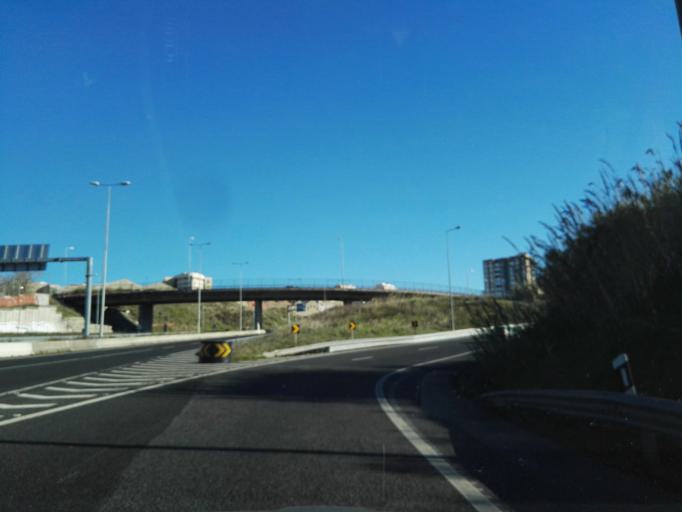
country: PT
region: Lisbon
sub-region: Odivelas
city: Pontinha
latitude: 38.7682
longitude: -9.2082
